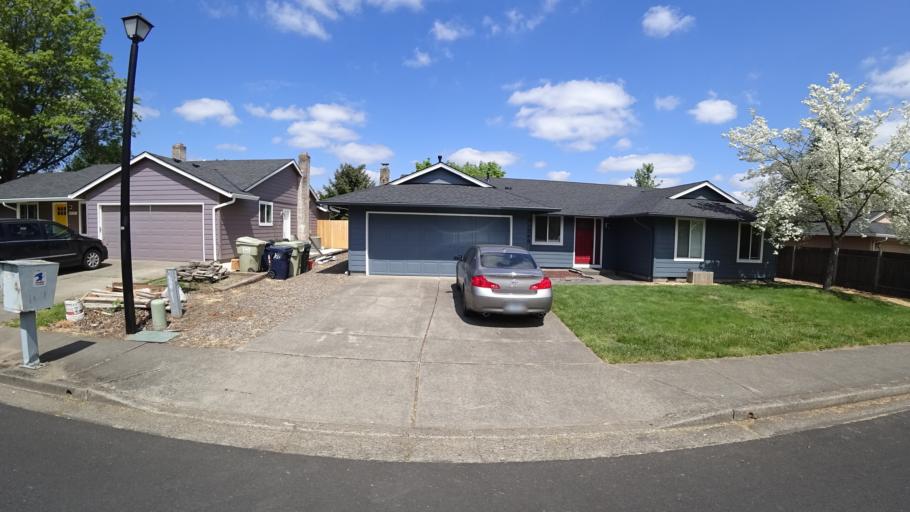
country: US
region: Oregon
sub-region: Washington County
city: Aloha
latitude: 45.5076
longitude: -122.8957
